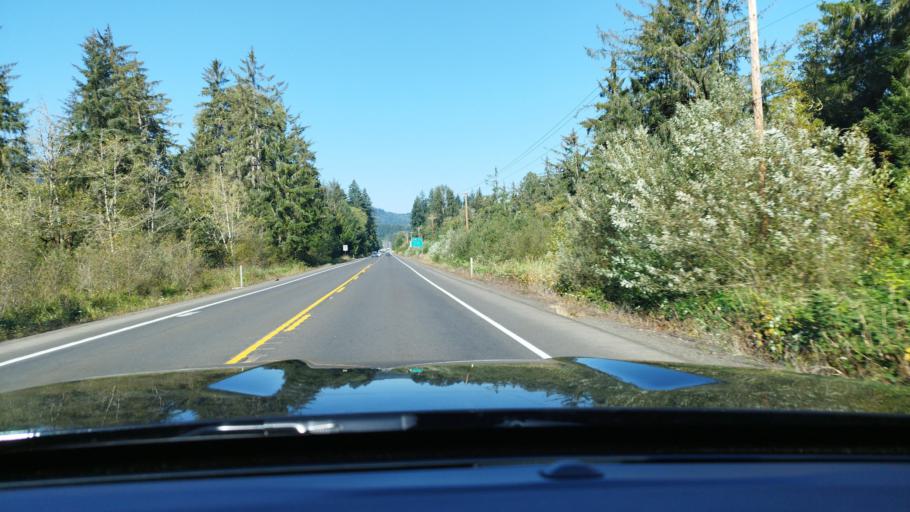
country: US
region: Washington
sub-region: Wahkiakum County
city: Cathlamet
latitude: 46.1430
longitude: -123.3959
